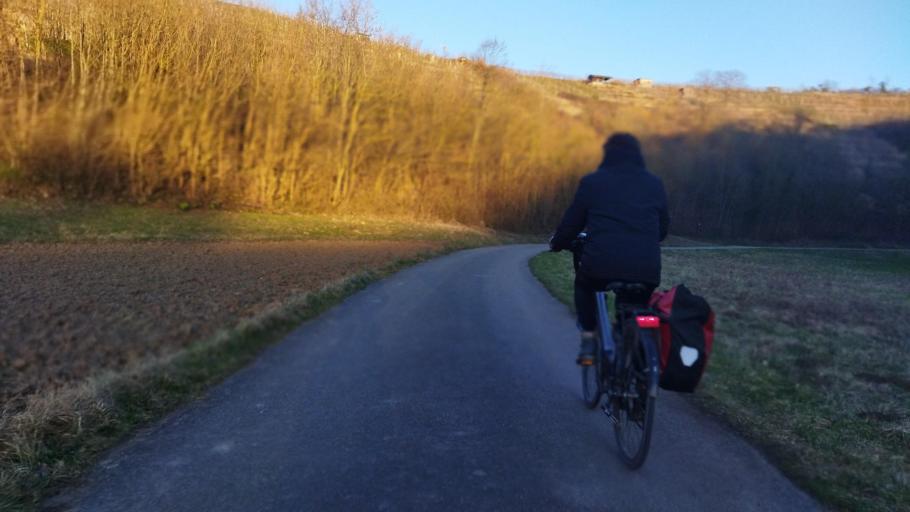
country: DE
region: Baden-Wuerttemberg
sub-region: Regierungsbezirk Stuttgart
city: Besigheim
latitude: 49.0116
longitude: 9.1353
